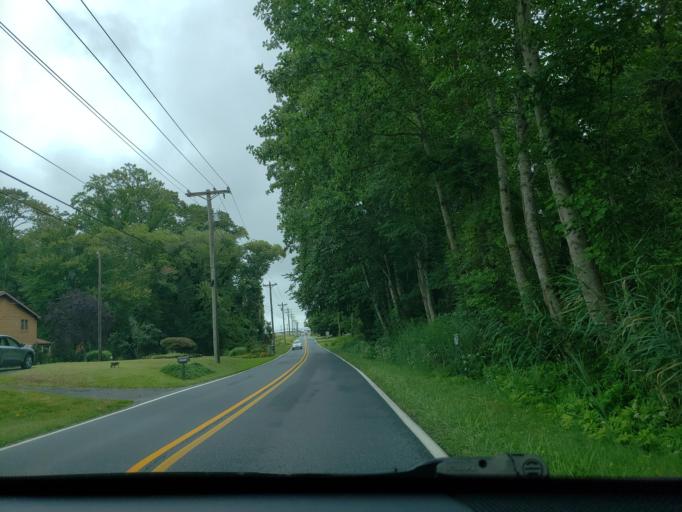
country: US
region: Delaware
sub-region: Sussex County
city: Lewes
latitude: 38.7518
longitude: -75.1559
